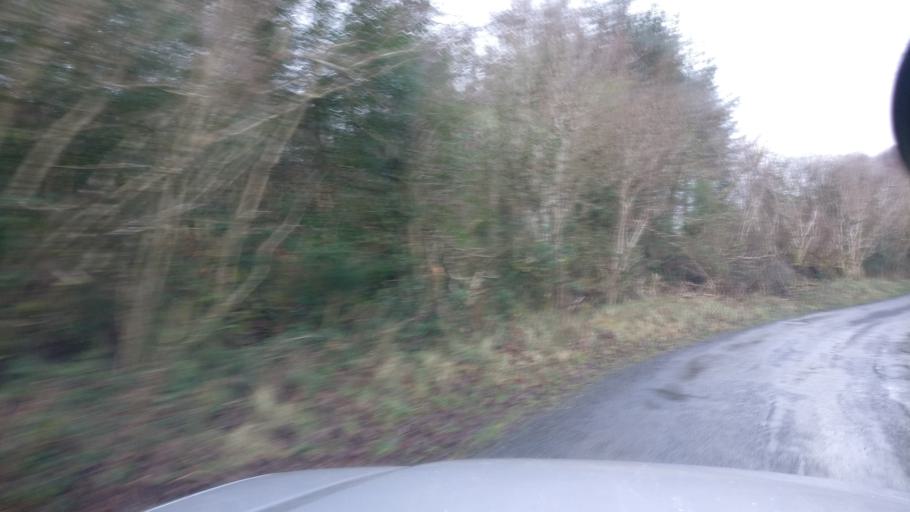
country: IE
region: Connaught
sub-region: County Galway
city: Loughrea
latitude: 53.1494
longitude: -8.6141
